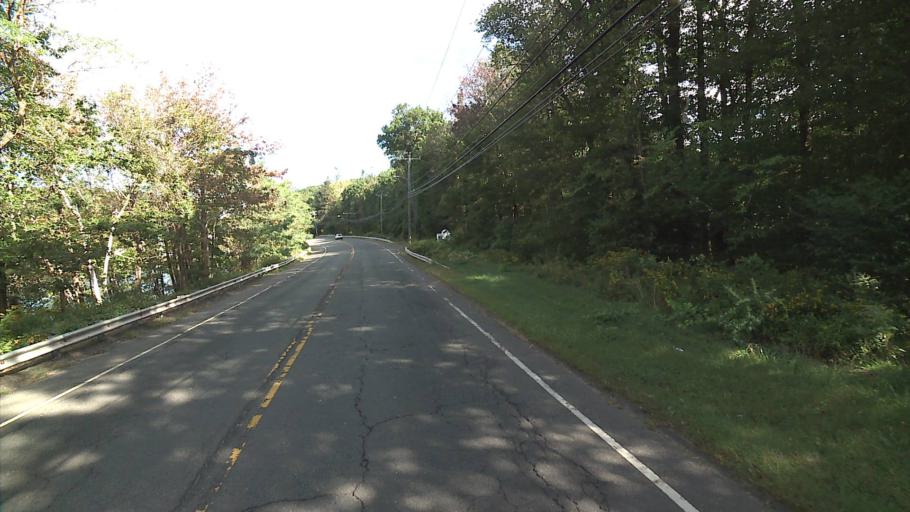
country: US
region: Connecticut
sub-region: Hartford County
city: Bristol
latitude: 41.6471
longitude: -72.9637
